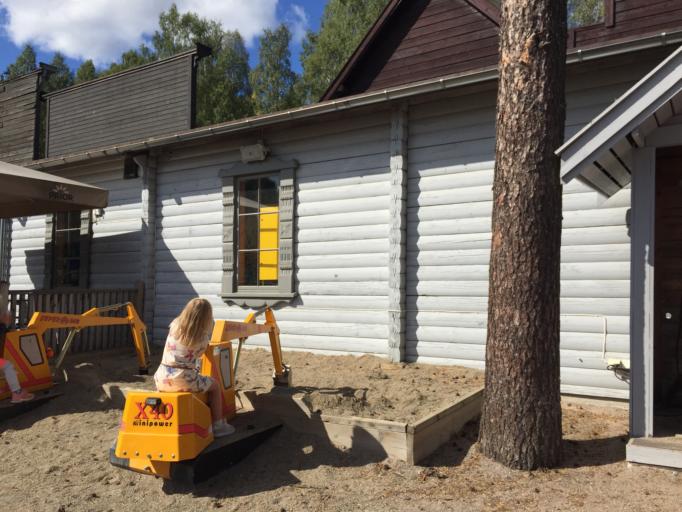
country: NO
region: Akershus
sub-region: Ski
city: Ski
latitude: 59.7458
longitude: 10.7748
